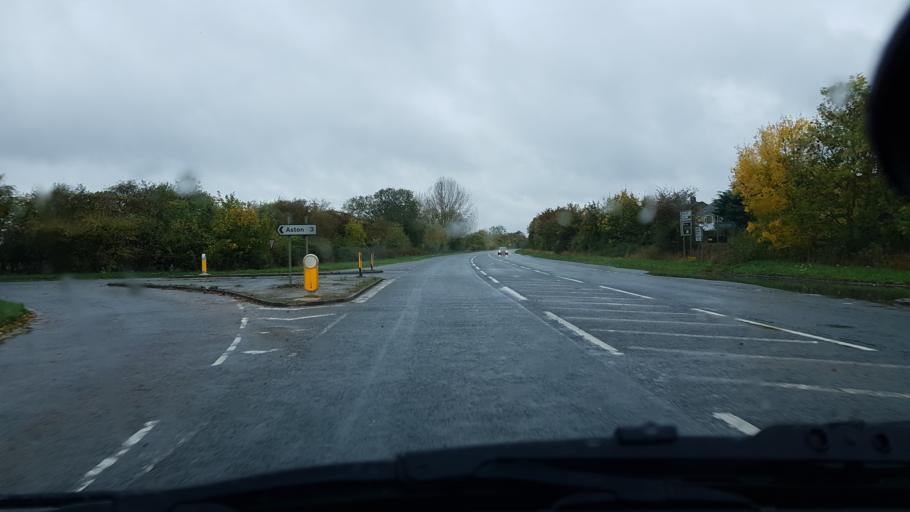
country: GB
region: England
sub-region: Oxfordshire
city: Ducklington
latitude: 51.7638
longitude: -1.4838
